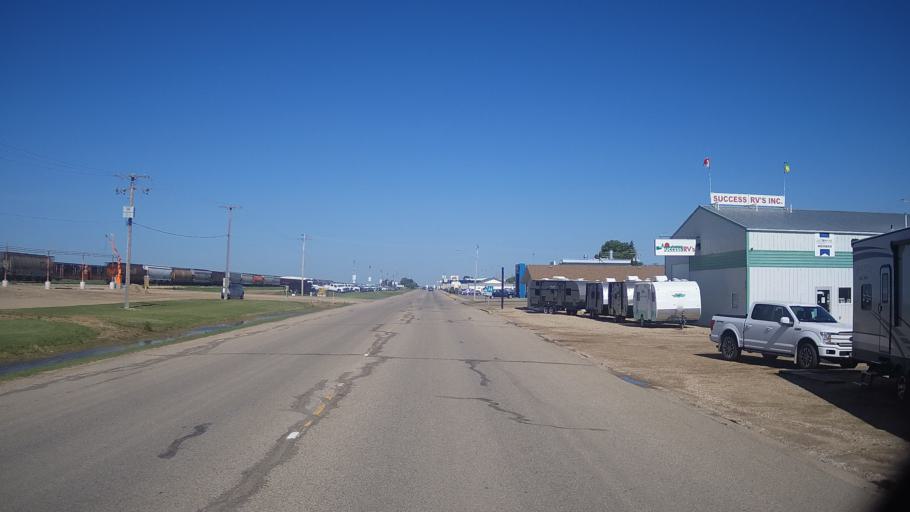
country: CA
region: Saskatchewan
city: Watrous
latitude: 51.6683
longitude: -105.4585
